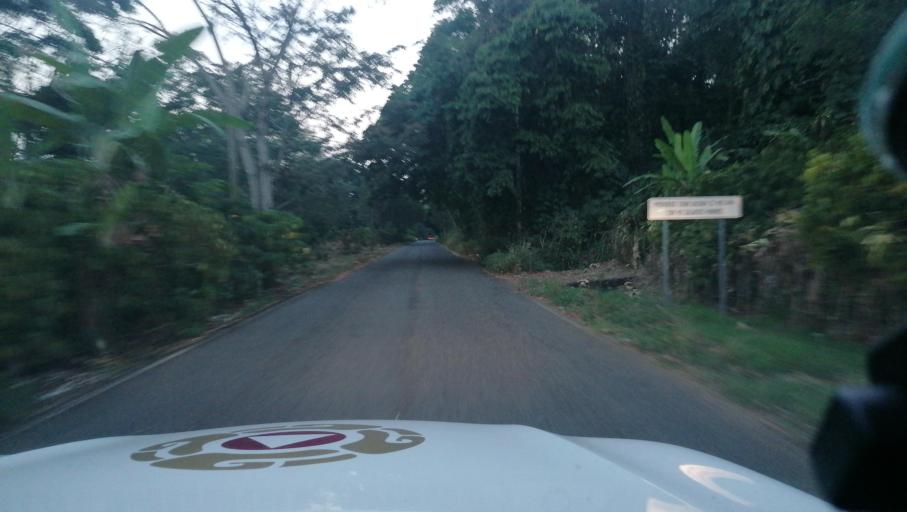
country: MX
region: Chiapas
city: Veinte de Noviembre
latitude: 15.0180
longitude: -92.2450
